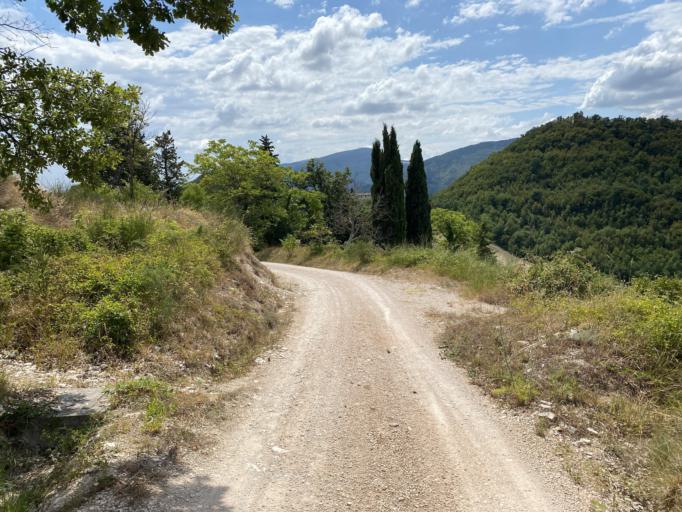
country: IT
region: The Marches
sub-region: Provincia di Pesaro e Urbino
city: Canavaccio
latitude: 43.7060
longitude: 12.7141
